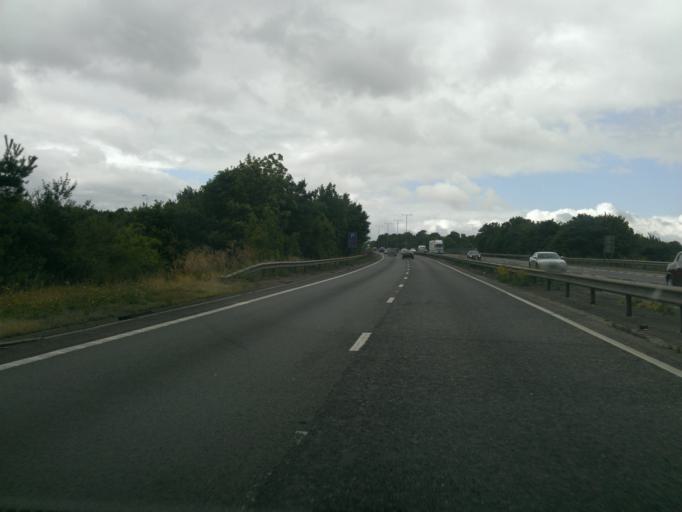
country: GB
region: England
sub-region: Essex
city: West Bergholt
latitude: 51.8966
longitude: 0.8578
